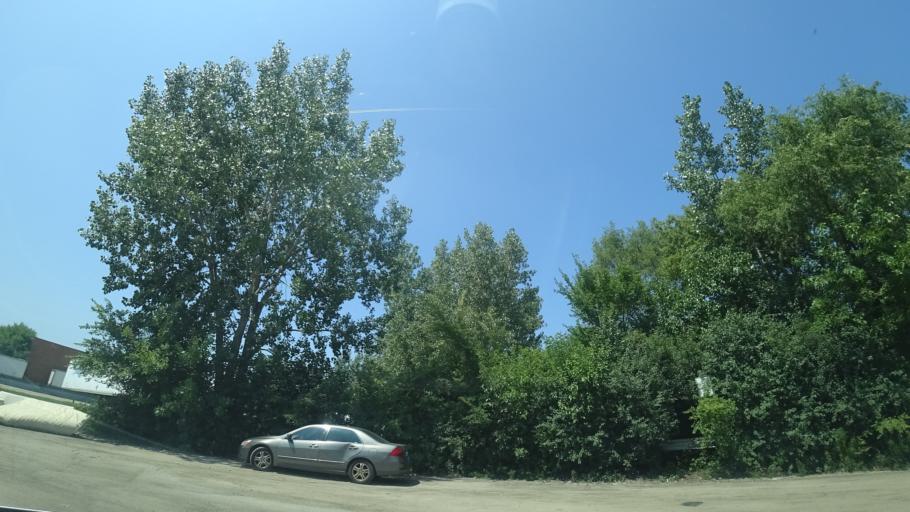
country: US
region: Illinois
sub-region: Cook County
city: Oak Lawn
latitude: 41.6939
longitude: -87.7571
